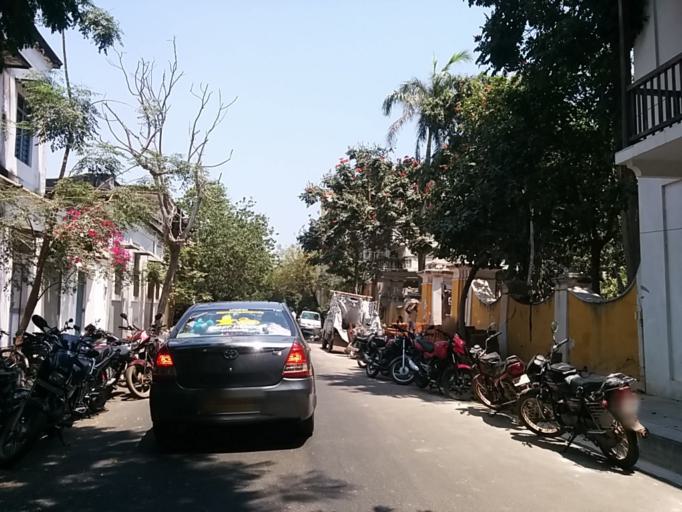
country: IN
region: Pondicherry
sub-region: Puducherry
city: Puducherry
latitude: 11.9266
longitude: 79.8340
